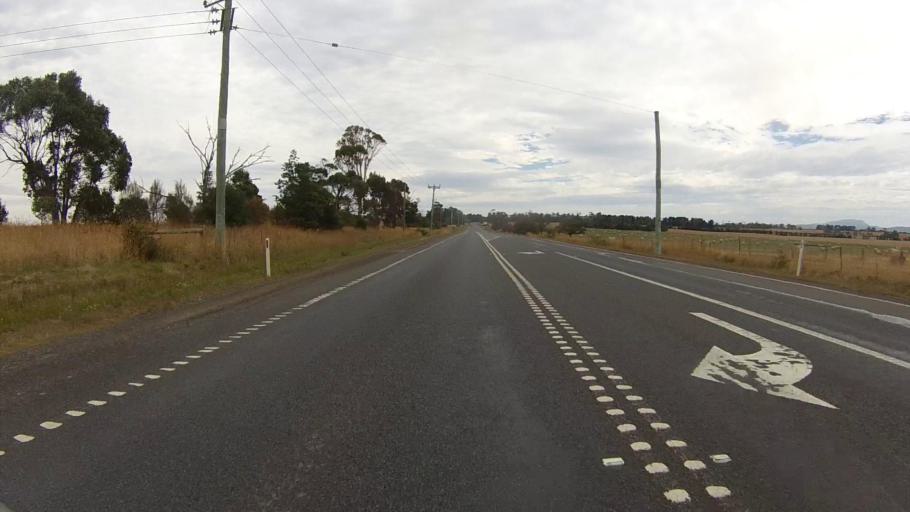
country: AU
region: Tasmania
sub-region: Northern Midlands
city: Evandale
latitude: -41.6139
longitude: 147.2236
